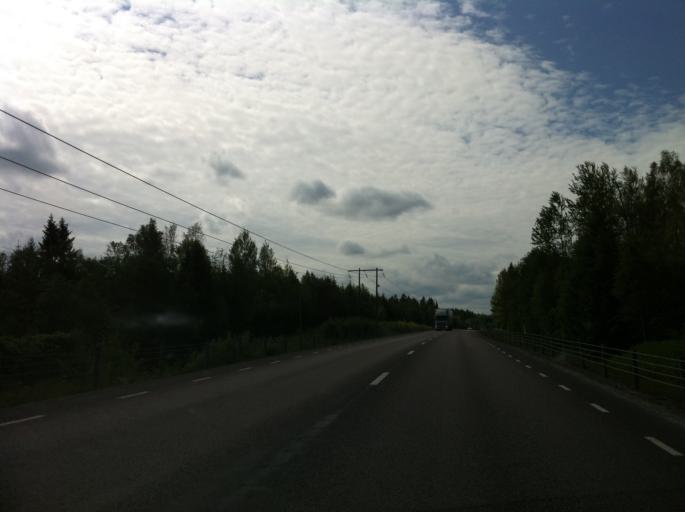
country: SE
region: Vaermland
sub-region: Karlstads Kommun
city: Edsvalla
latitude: 59.4374
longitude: 13.2018
